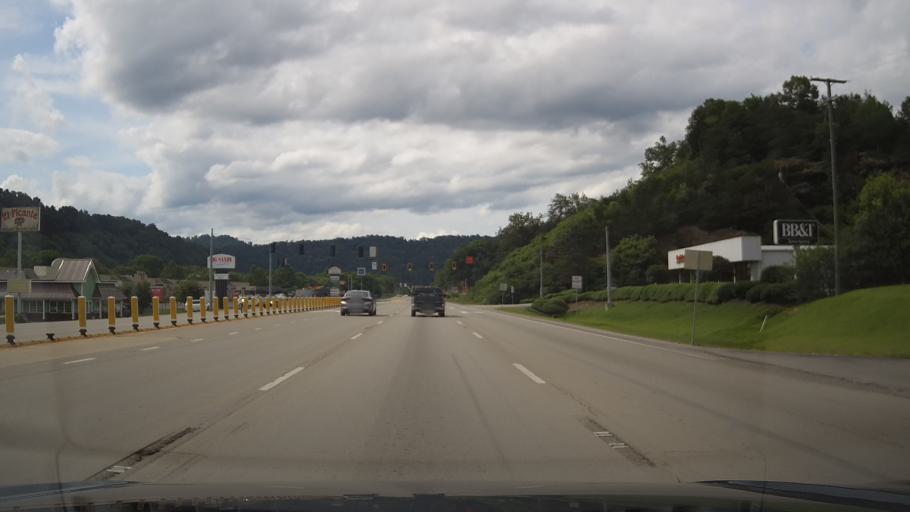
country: US
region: Kentucky
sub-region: Pike County
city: Coal Run Village
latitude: 37.5256
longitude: -82.5732
